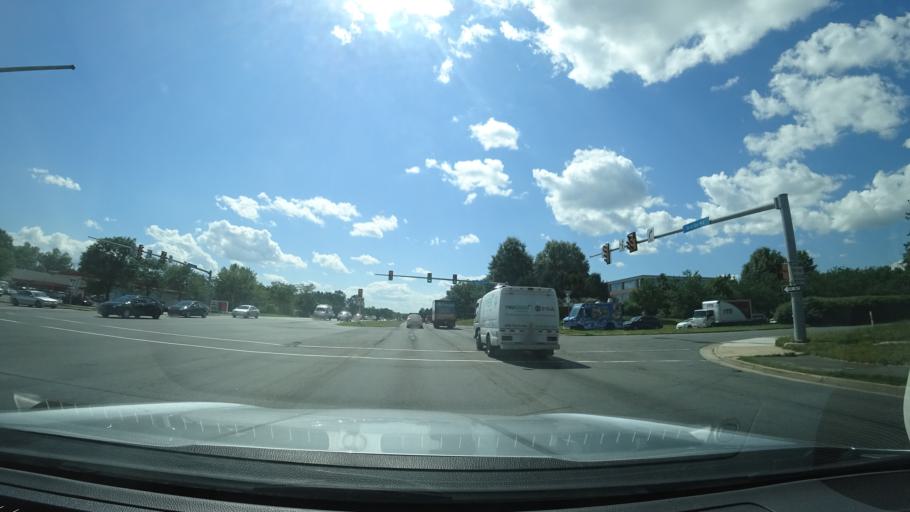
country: US
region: Virginia
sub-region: Loudoun County
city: Sterling
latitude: 38.9792
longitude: -77.4339
